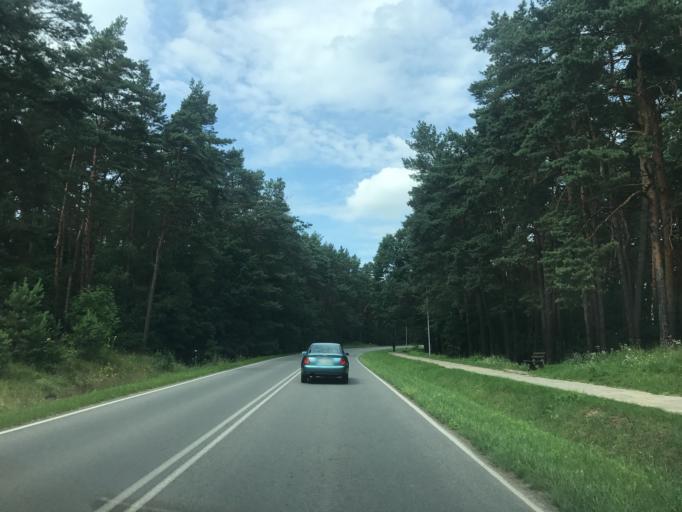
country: PL
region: West Pomeranian Voivodeship
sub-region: Powiat goleniowski
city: Goleniow
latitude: 53.5616
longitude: 14.8155
